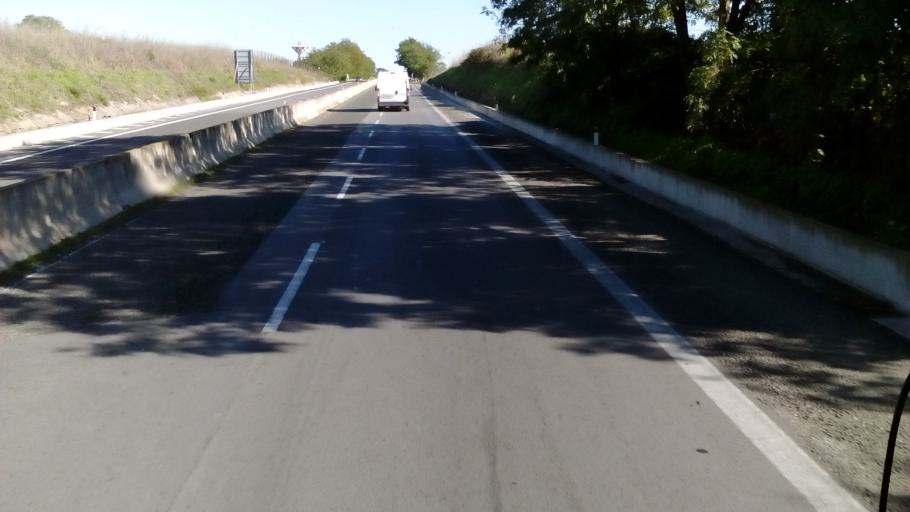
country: IT
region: Latium
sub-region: Provincia di Viterbo
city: Montalto di Castro
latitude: 42.3473
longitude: 11.6056
